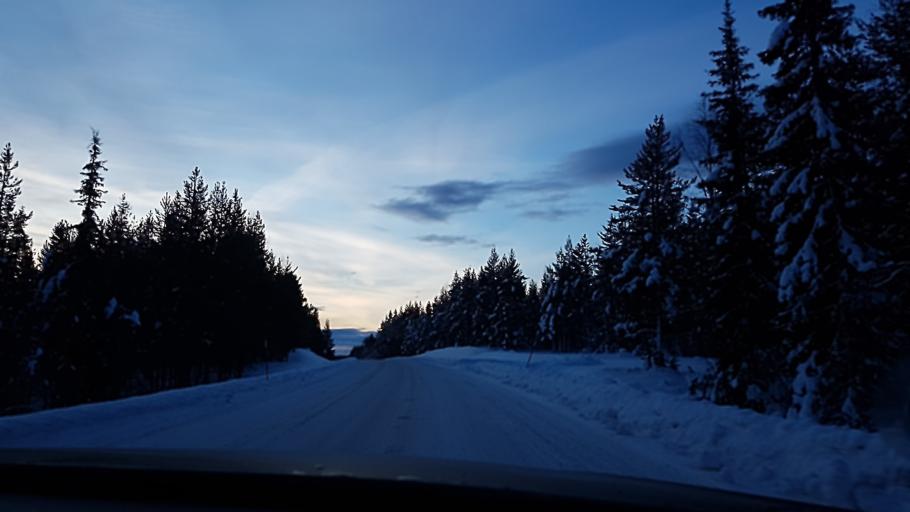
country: SE
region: Norrbotten
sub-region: Arvidsjaurs Kommun
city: Arvidsjaur
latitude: 65.9361
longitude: 19.4635
